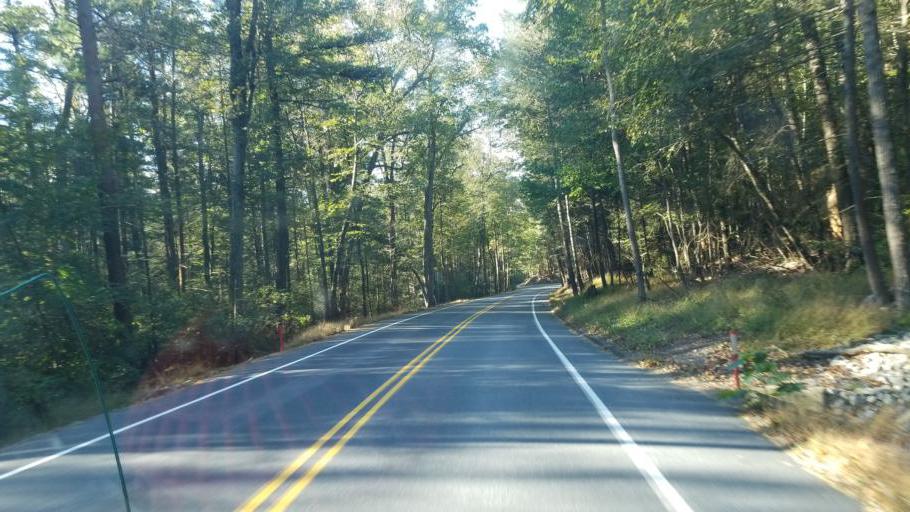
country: US
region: Pennsylvania
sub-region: Franklin County
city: Mont Alto
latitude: 39.8417
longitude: -77.5238
